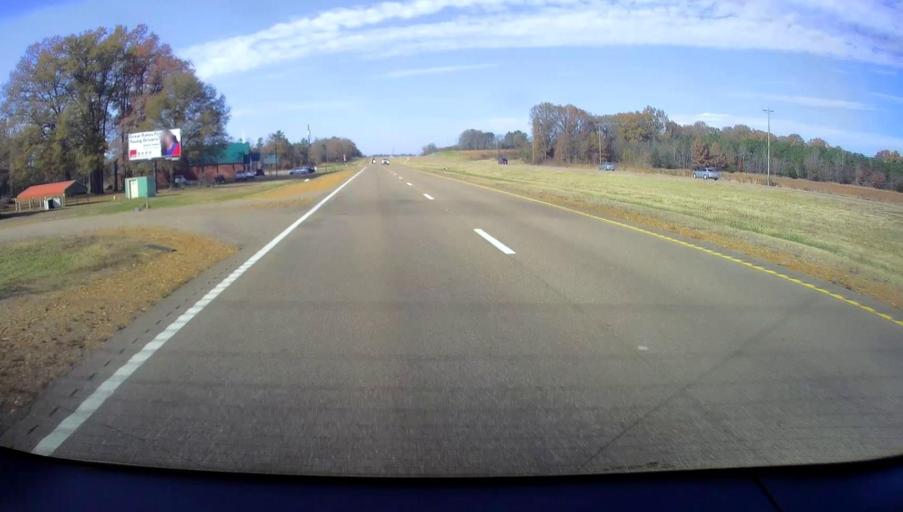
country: US
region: Tennessee
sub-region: Fayette County
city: Piperton
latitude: 34.9798
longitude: -89.5804
